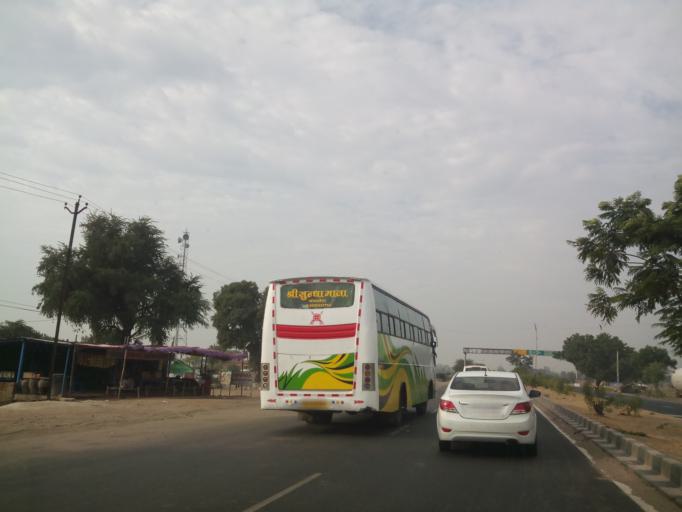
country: IN
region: Gujarat
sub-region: Ahmadabad
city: Dholka
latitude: 22.6388
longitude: 72.1935
